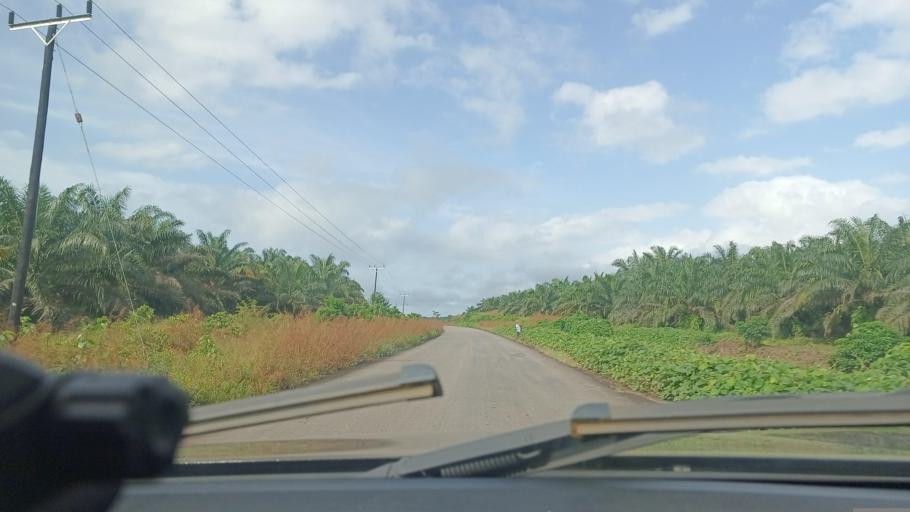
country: LR
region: Bomi
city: Tubmanburg
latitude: 6.7260
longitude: -11.0457
